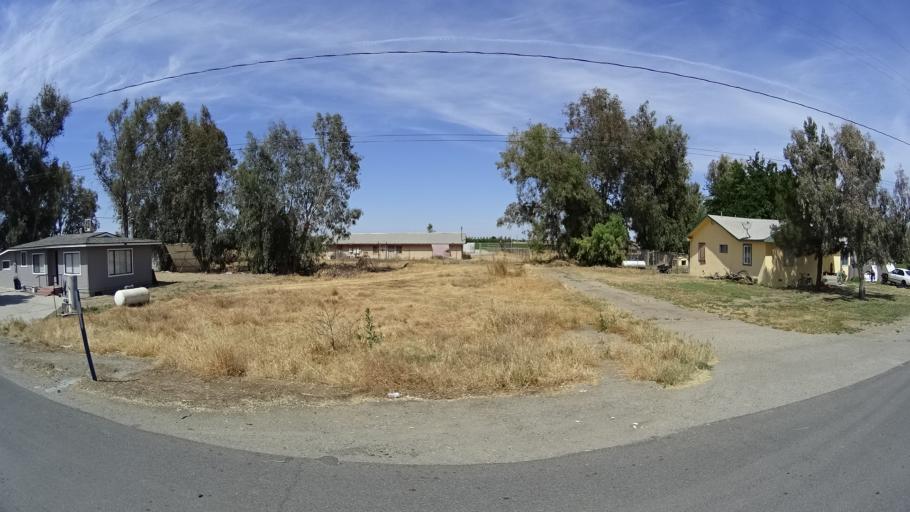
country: US
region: California
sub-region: Kings County
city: Hanford
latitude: 36.3414
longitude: -119.6010
